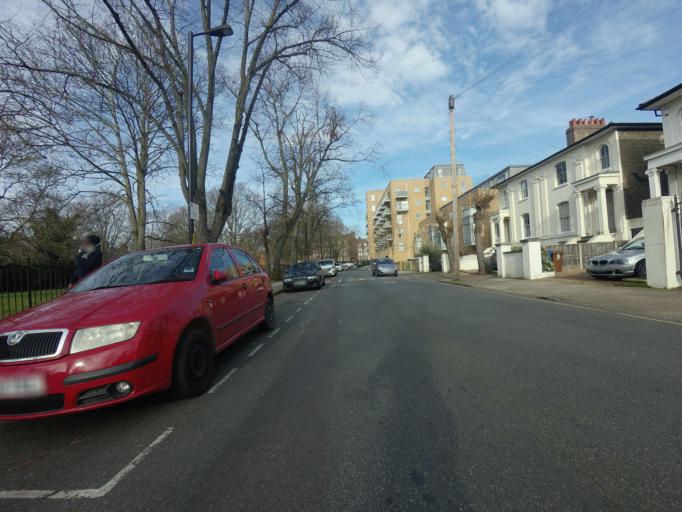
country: GB
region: England
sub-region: Greater London
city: Camberwell
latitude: 51.4852
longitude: -0.0726
